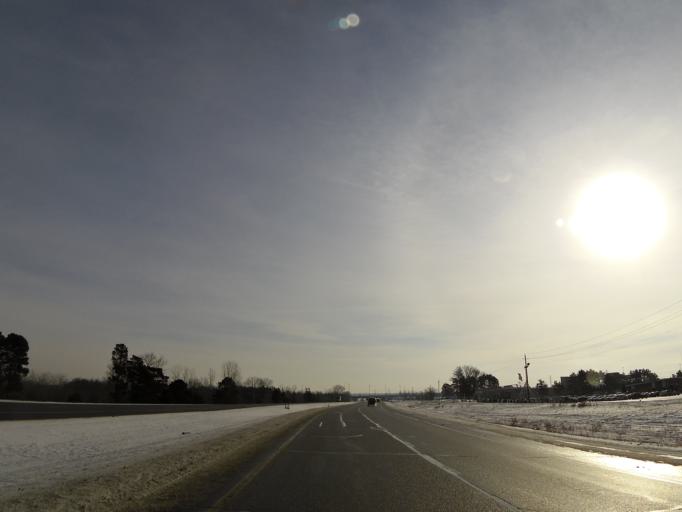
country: US
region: Minnesota
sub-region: Hennepin County
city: Eden Prairie
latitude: 44.7946
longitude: -93.4193
